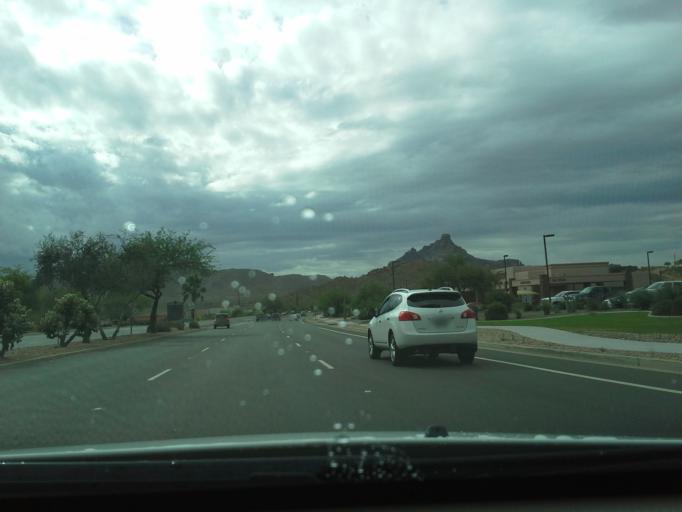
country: US
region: Arizona
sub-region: Maricopa County
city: Fountain Hills
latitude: 33.5727
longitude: -111.7137
